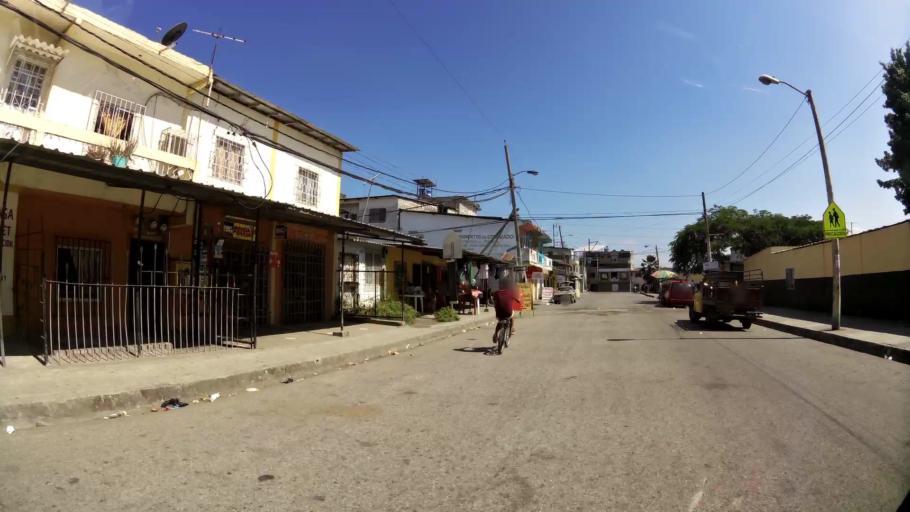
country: EC
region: Guayas
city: Guayaquil
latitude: -2.2285
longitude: -79.9403
